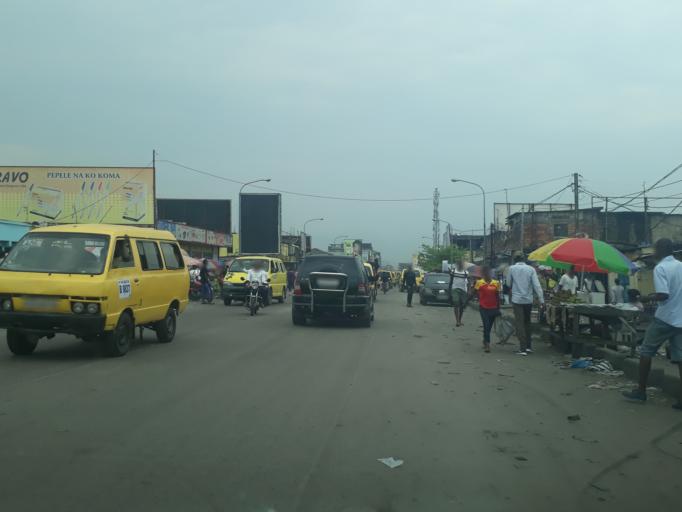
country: CD
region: Kinshasa
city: Kinshasa
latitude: -4.3467
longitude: 15.3119
